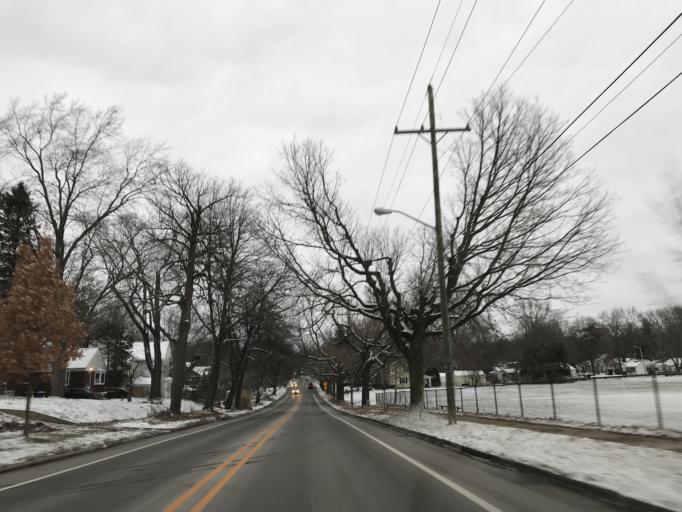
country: US
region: Michigan
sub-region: Washtenaw County
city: Ann Arbor
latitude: 42.2982
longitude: -83.7367
